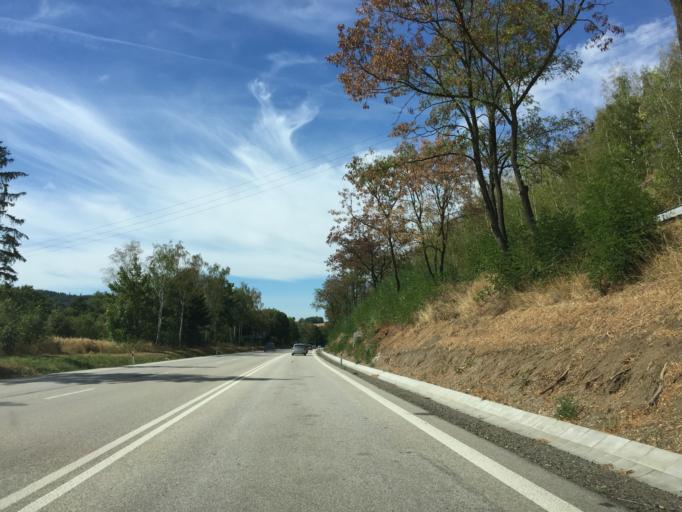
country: CZ
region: Central Bohemia
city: Votice
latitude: 49.6448
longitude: 14.6415
